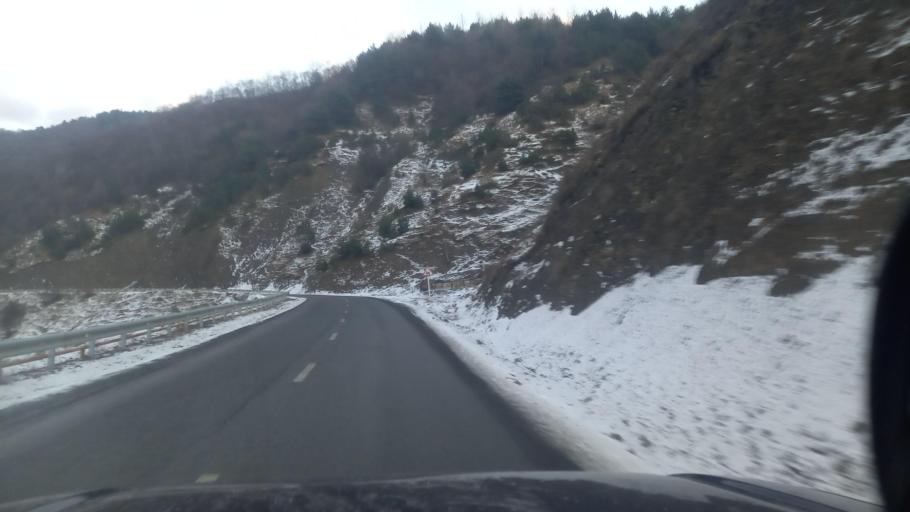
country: RU
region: Ingushetiya
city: Dzhayrakh
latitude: 42.8109
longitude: 44.8030
